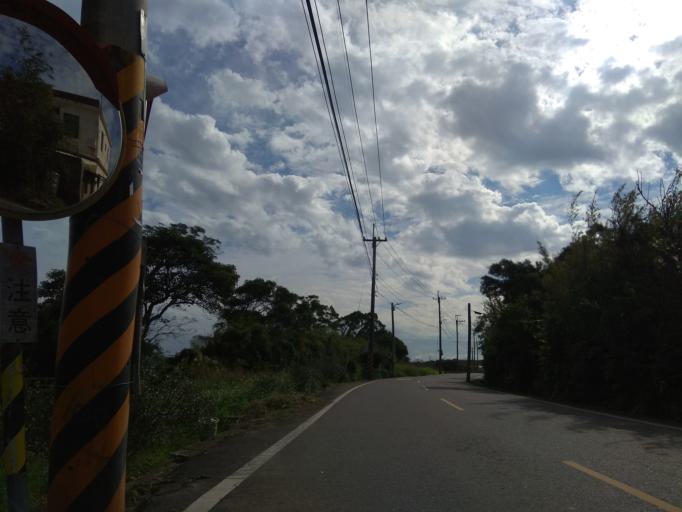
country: TW
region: Taiwan
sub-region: Hsinchu
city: Zhubei
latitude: 24.9589
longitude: 121.1071
